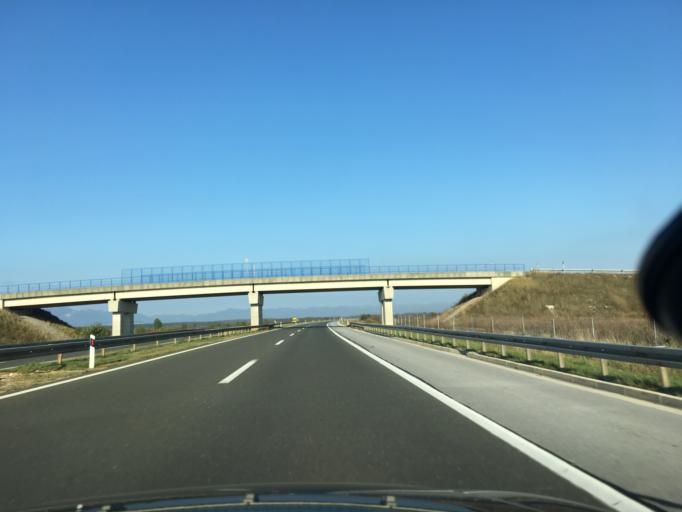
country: HR
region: Licko-Senjska
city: Gospic
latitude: 44.4798
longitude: 15.5642
